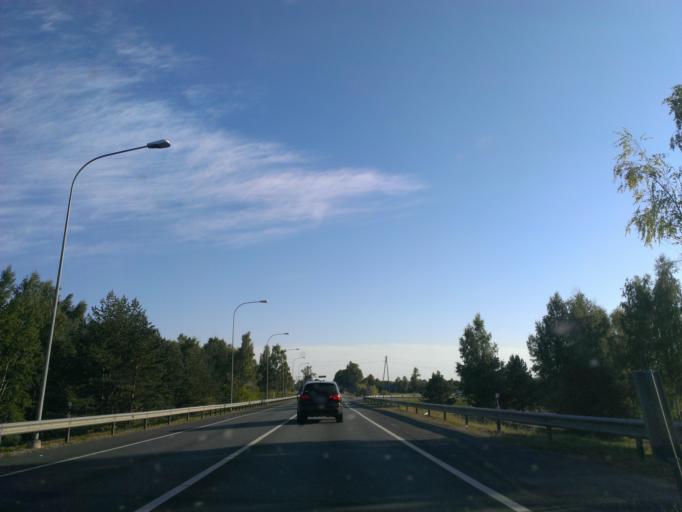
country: LV
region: Adazi
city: Adazi
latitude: 57.1189
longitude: 24.3248
